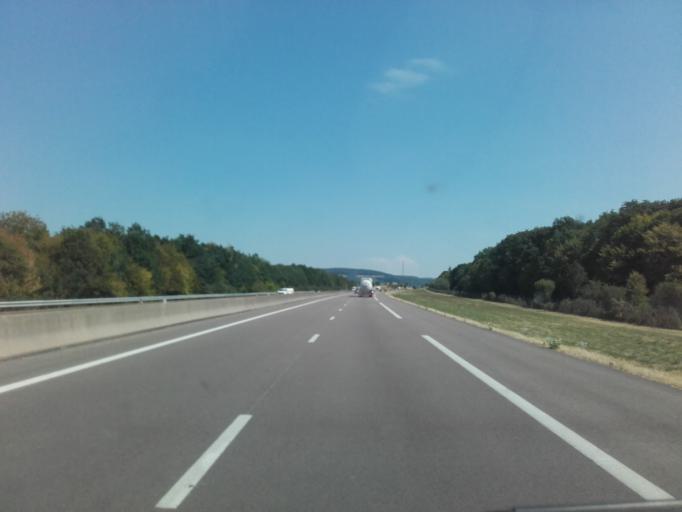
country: FR
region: Bourgogne
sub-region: Departement de la Cote-d'Or
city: Vitteaux
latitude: 47.3526
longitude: 4.4461
